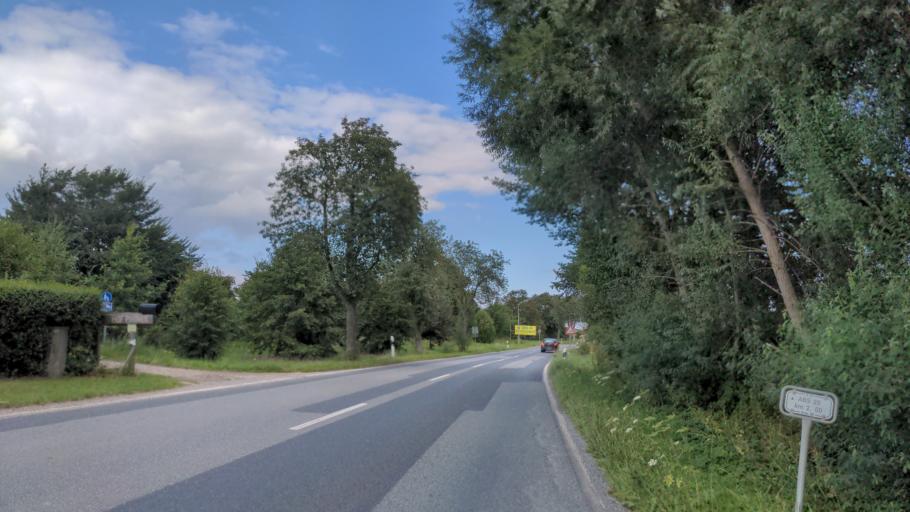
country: DE
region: Schleswig-Holstein
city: Beschendorf
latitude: 54.1777
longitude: 10.8764
